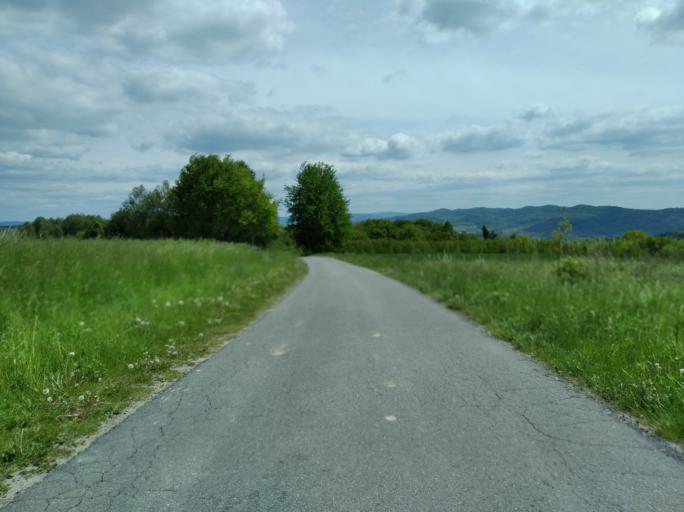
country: PL
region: Subcarpathian Voivodeship
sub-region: Powiat strzyzowski
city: Wisniowa
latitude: 49.8907
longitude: 21.6223
